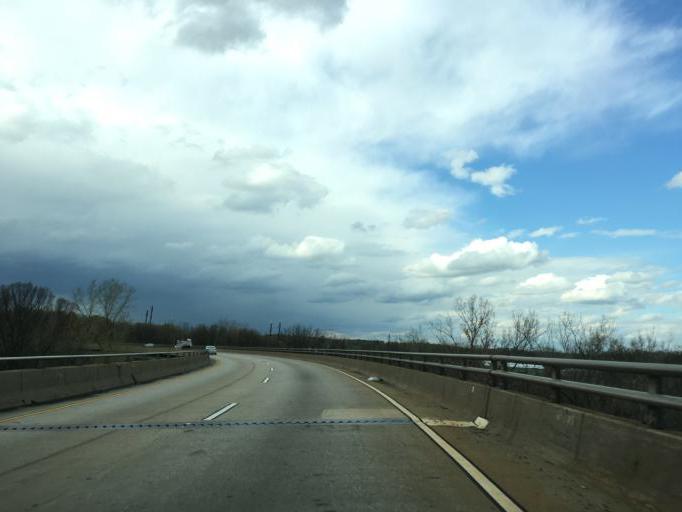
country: US
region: Maryland
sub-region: Baltimore County
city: Essex
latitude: 39.3238
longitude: -76.4779
